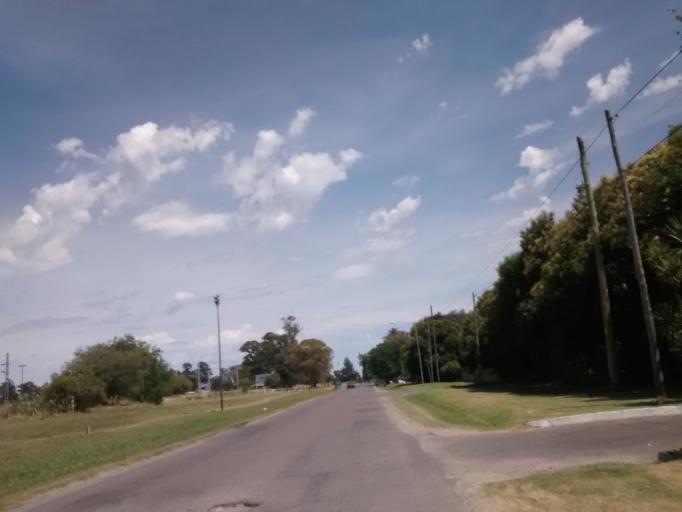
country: AR
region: Buenos Aires
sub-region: Partido de La Plata
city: La Plata
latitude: -34.8705
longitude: -58.0311
